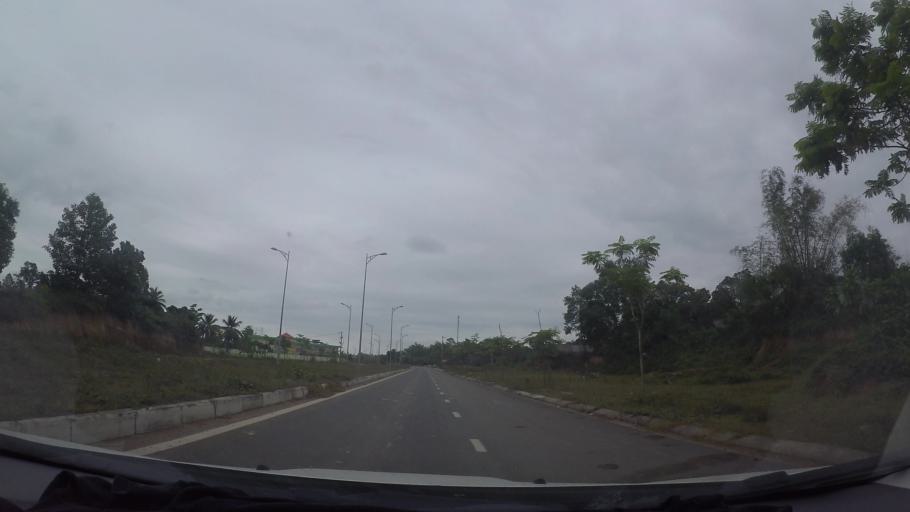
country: VN
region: Da Nang
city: Lien Chieu
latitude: 16.0774
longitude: 108.0945
